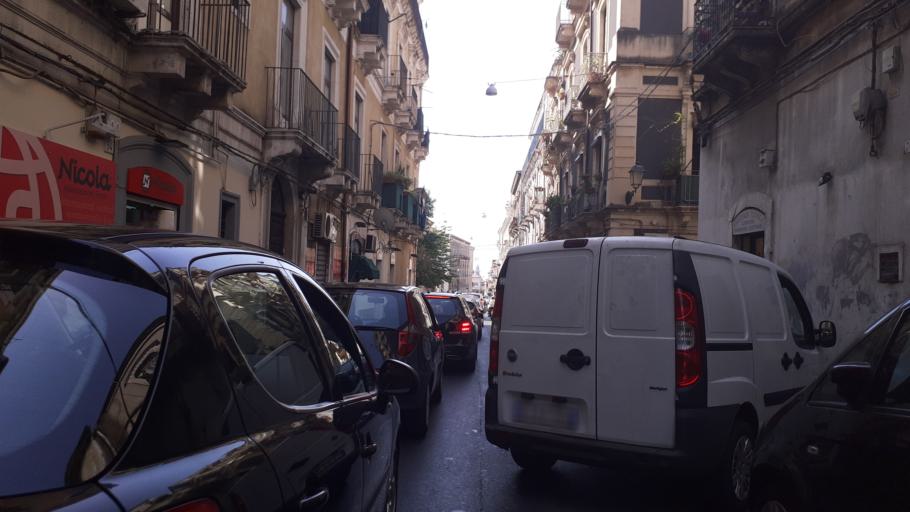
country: IT
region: Sicily
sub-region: Catania
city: Catania
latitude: 37.5059
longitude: 15.0932
